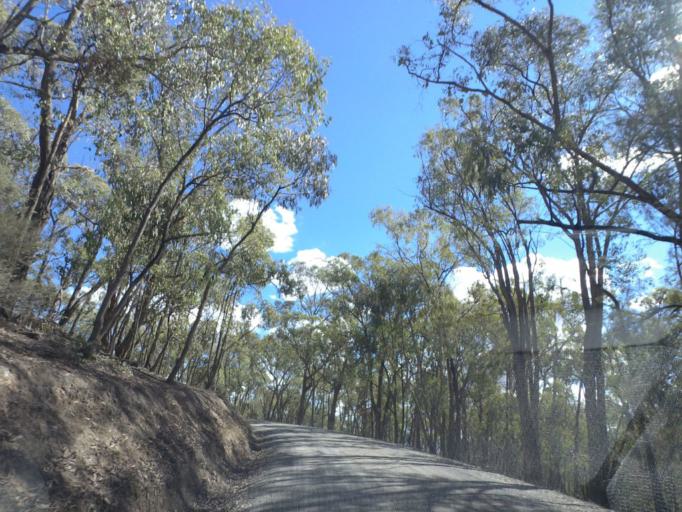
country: AU
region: Victoria
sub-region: Murrindindi
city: Alexandra
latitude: -37.3081
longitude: 145.8200
